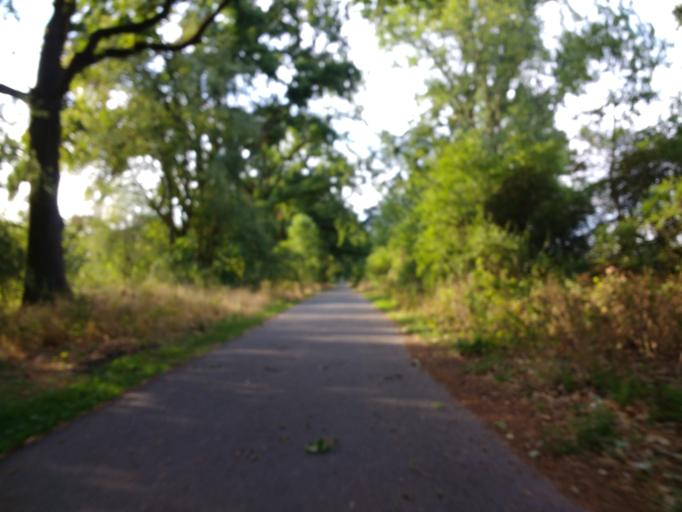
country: DE
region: Lower Saxony
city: Gifhorn
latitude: 52.4490
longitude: 10.5573
